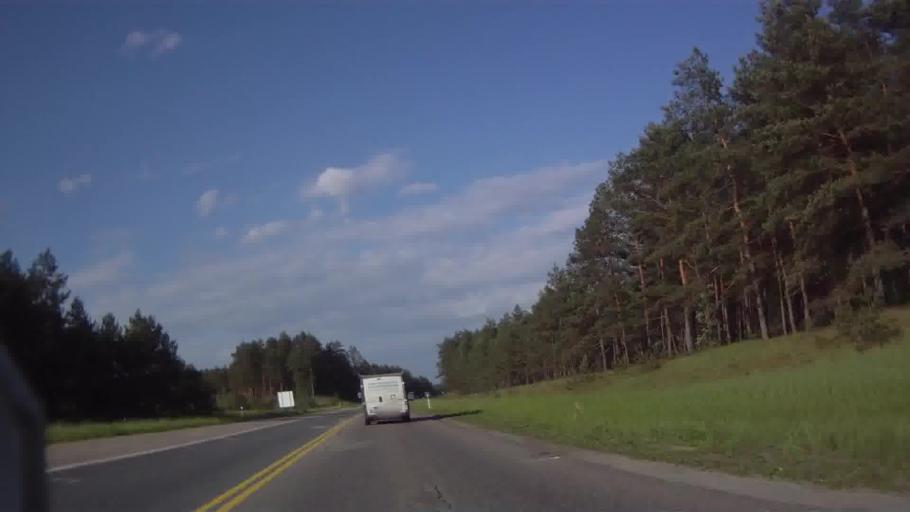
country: LV
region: Garkalne
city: Garkalne
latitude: 57.0611
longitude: 24.4625
